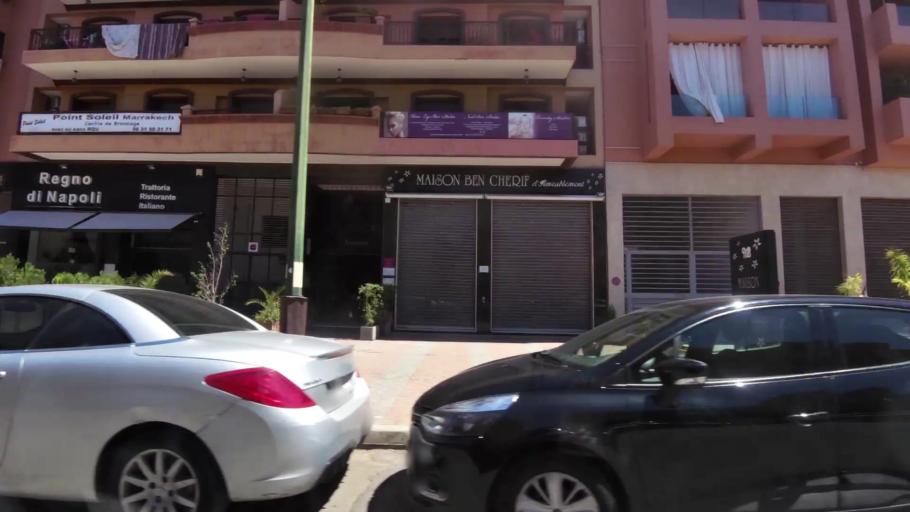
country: MA
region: Marrakech-Tensift-Al Haouz
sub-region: Marrakech
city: Marrakesh
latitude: 31.6283
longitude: -8.0071
